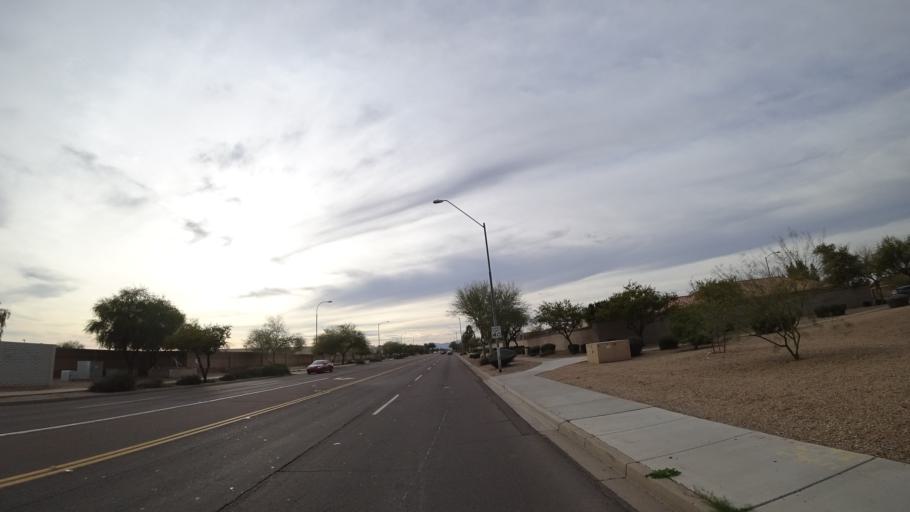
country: US
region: Arizona
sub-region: Maricopa County
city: Peoria
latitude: 33.5668
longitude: -112.2287
